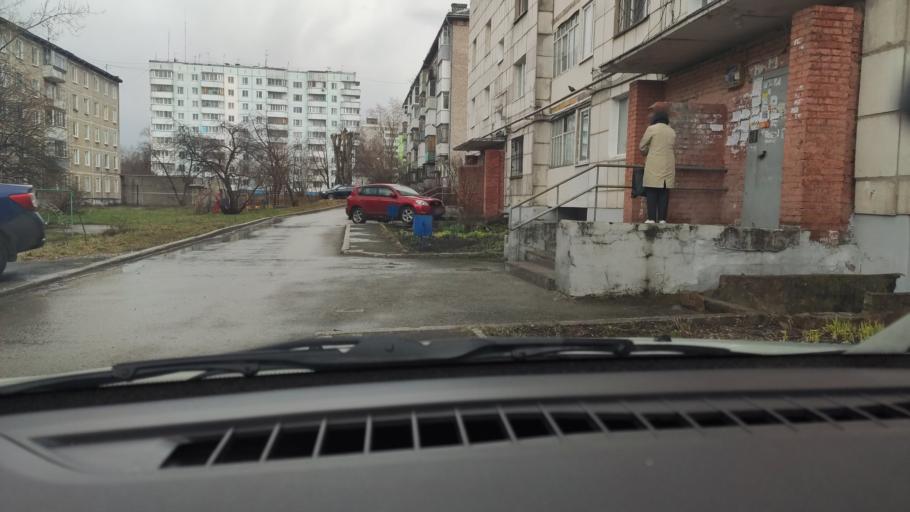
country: RU
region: Perm
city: Perm
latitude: 58.1140
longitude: 56.3712
